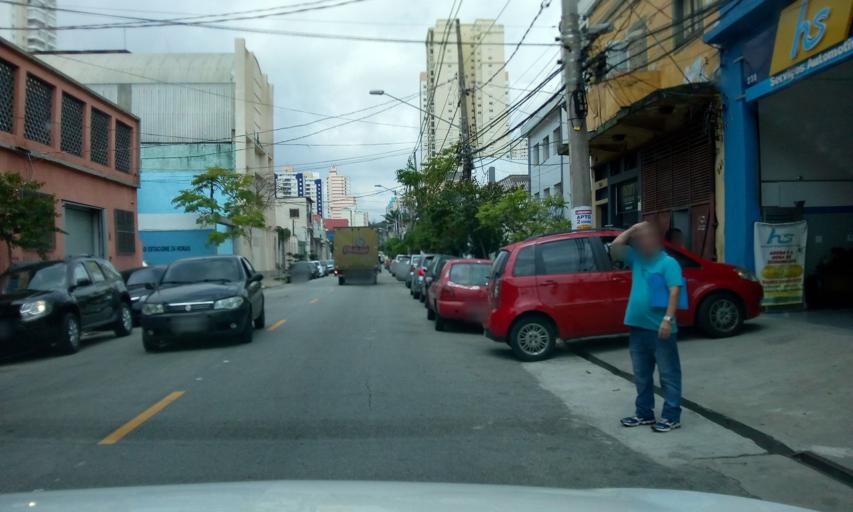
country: BR
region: Sao Paulo
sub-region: Sao Paulo
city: Sao Paulo
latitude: -23.5653
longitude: -46.6249
